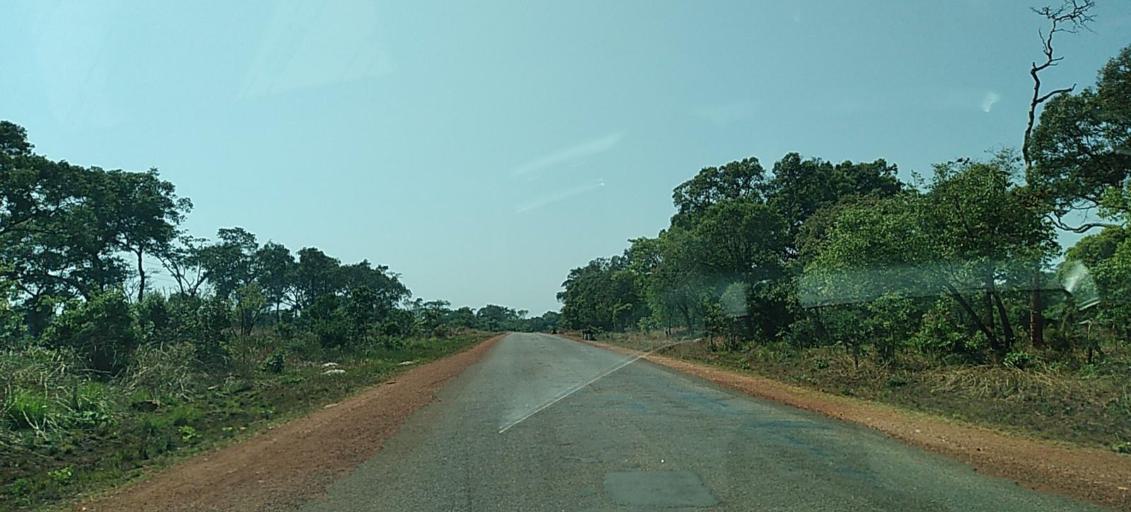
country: ZM
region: North-Western
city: Solwezi
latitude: -12.1323
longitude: 25.5308
